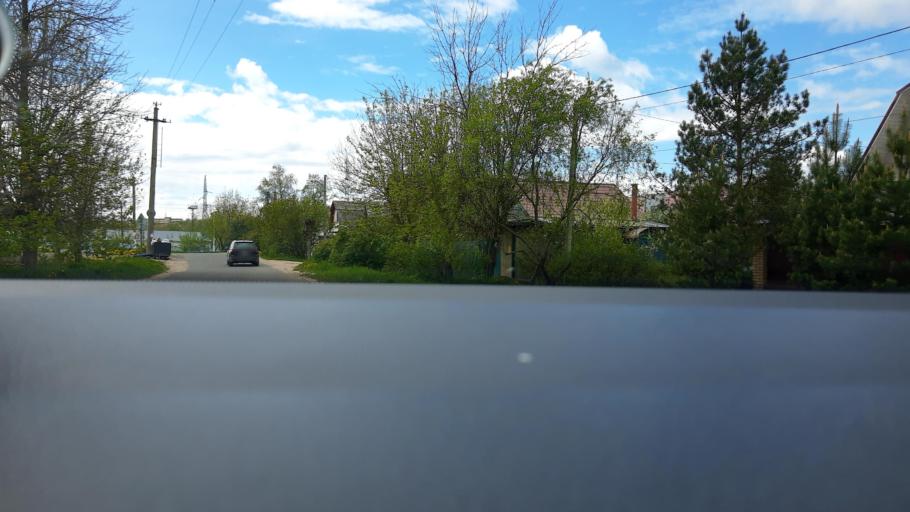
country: RU
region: Moskovskaya
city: Dmitrov
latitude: 56.3541
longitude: 37.5436
